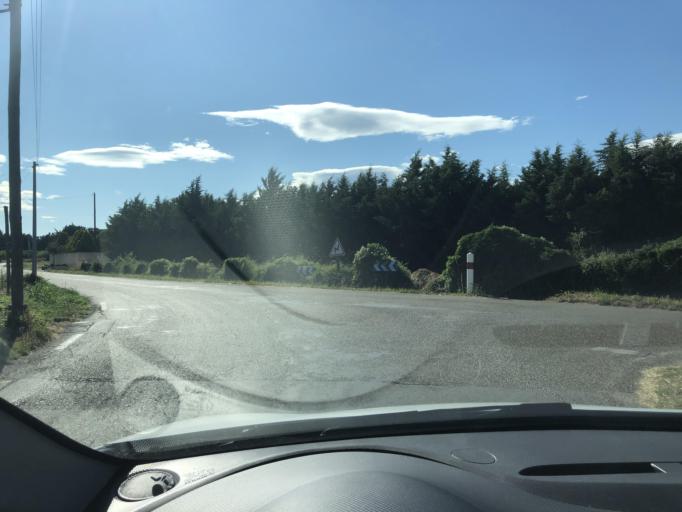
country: FR
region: Provence-Alpes-Cote d'Azur
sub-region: Departement des Bouches-du-Rhone
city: Chateaurenard
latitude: 43.8966
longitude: 4.8397
